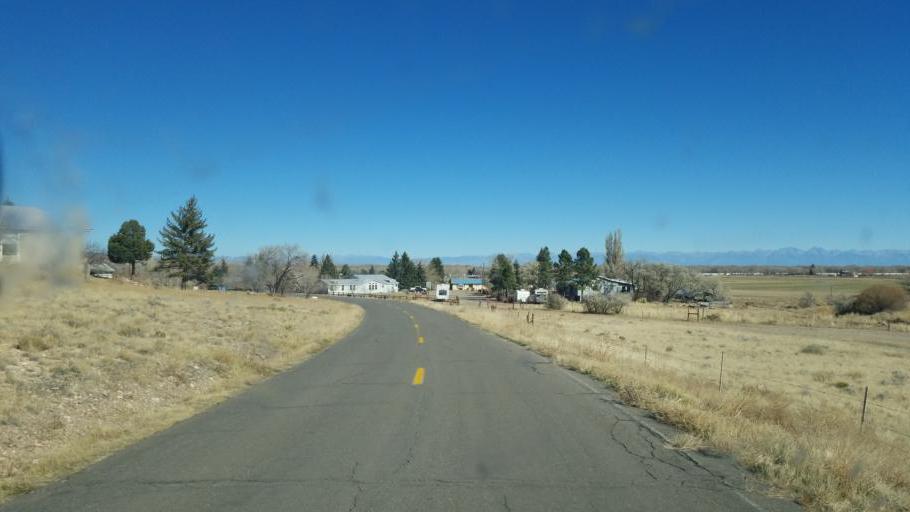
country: US
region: Colorado
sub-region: Rio Grande County
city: Del Norte
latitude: 37.6681
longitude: -106.3468
